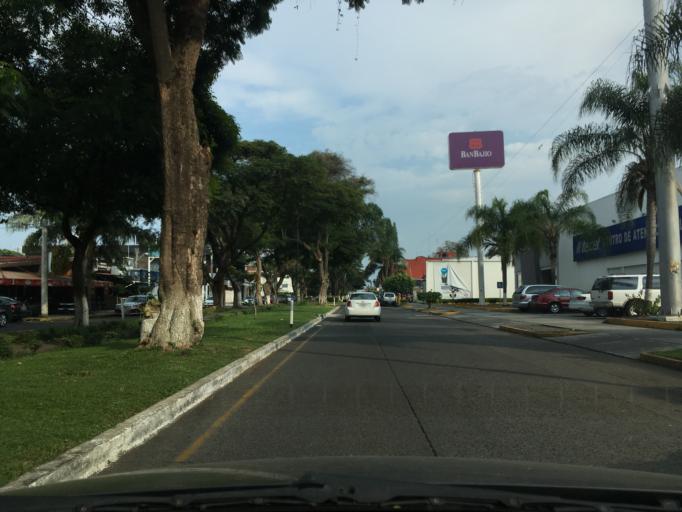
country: MX
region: Michoacan
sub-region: Uruapan
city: Uruapan
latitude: 19.4072
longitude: -102.0569
